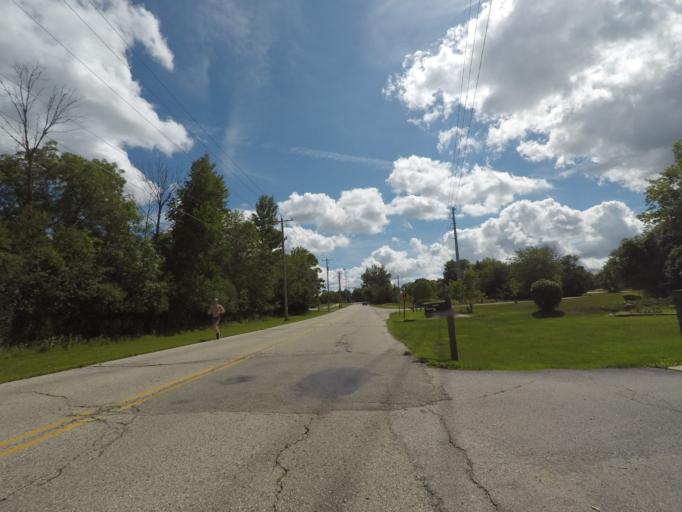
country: US
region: Wisconsin
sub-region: Waukesha County
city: Pewaukee
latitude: 43.0572
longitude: -88.3080
